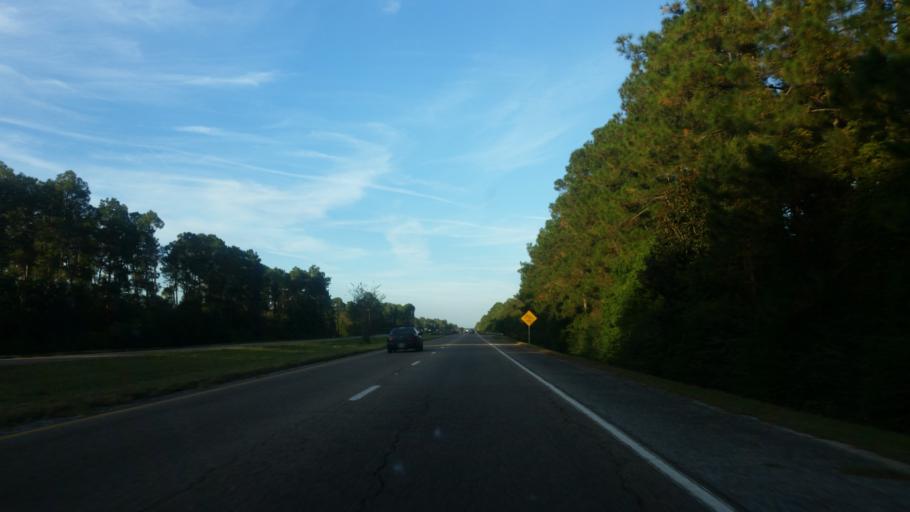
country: US
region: Mississippi
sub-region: Jackson County
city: Helena
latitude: 30.4358
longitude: -88.4378
